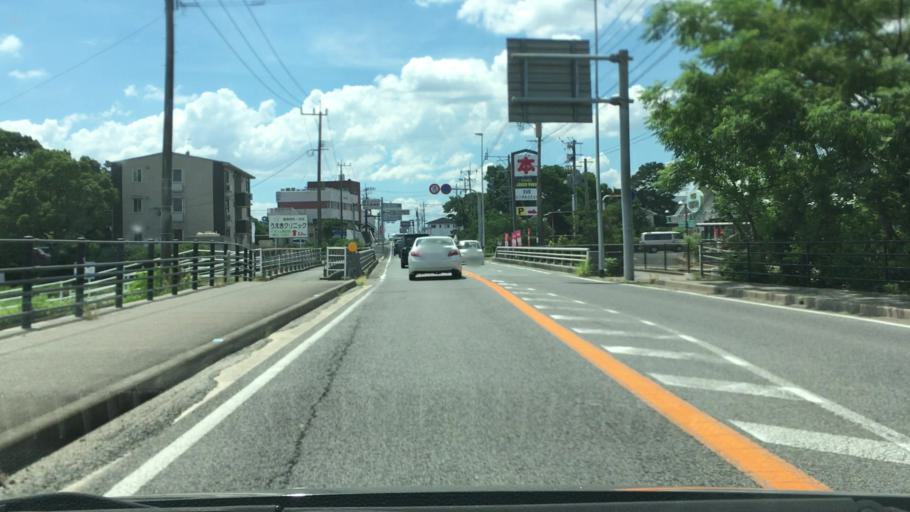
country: JP
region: Saga Prefecture
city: Tosu
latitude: 33.3442
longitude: 130.4453
